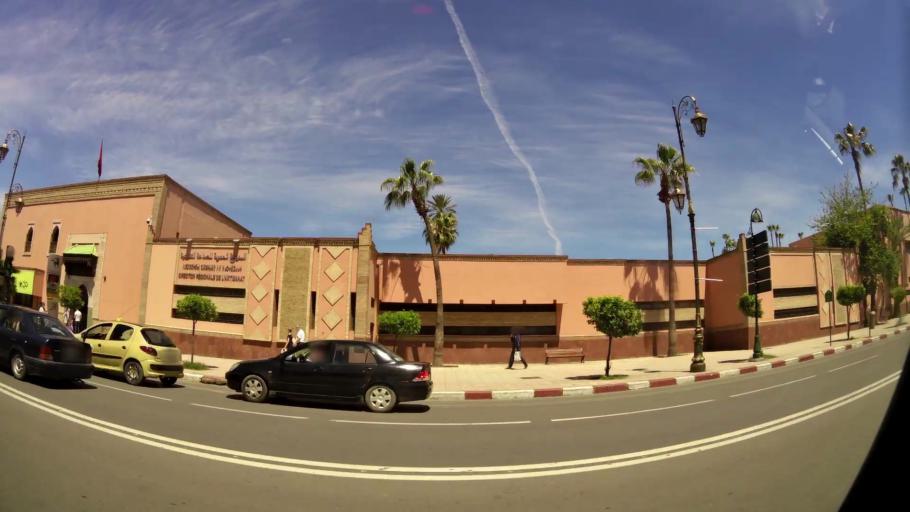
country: MA
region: Marrakech-Tensift-Al Haouz
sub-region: Marrakech
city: Marrakesh
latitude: 31.6269
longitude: -7.9964
